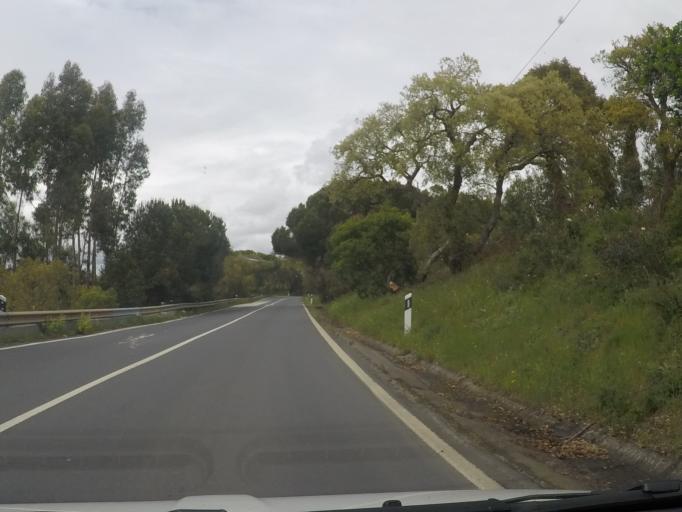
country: PT
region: Setubal
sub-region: Sines
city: Porto Covo
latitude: 37.8710
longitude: -8.7438
